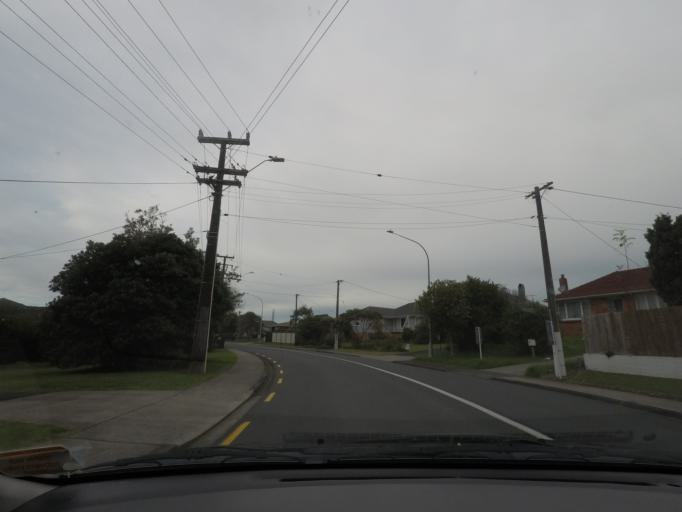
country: NZ
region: Auckland
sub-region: Auckland
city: Rosebank
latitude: -36.8632
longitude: 174.6438
